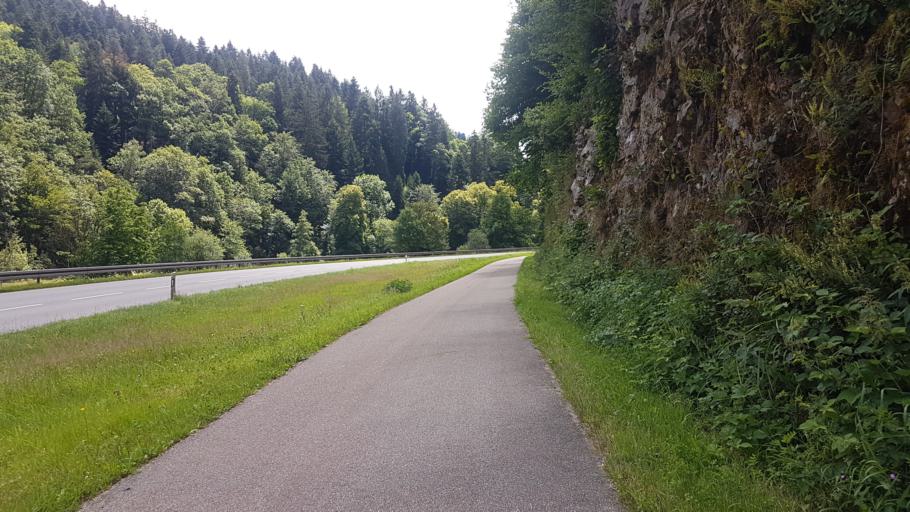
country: DE
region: Baden-Wuerttemberg
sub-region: Freiburg Region
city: Schramberg
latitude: 48.2500
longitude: 8.3727
